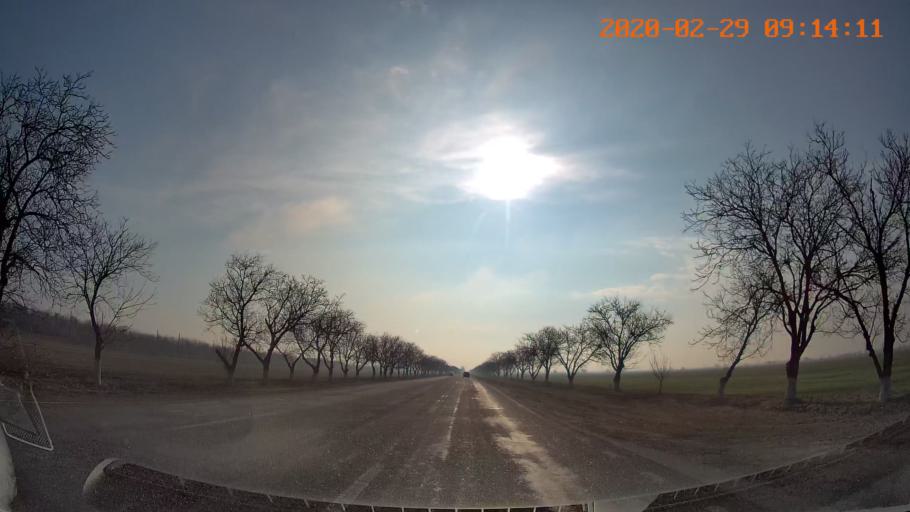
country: MD
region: Telenesti
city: Pervomaisc
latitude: 46.8108
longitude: 29.8486
